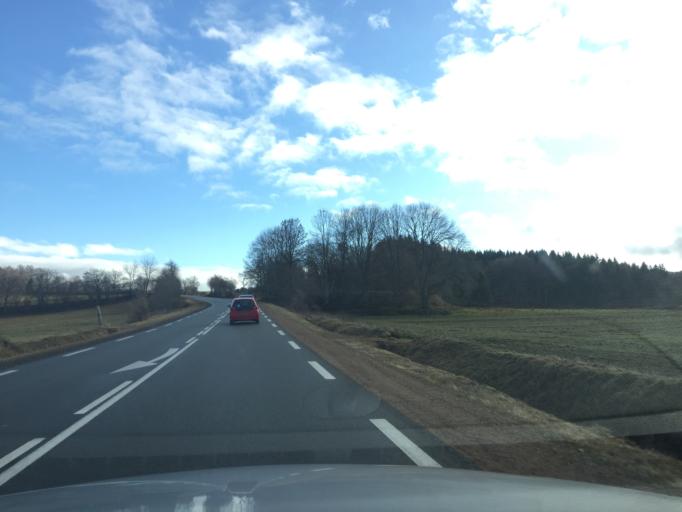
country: FR
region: Auvergne
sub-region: Departement du Puy-de-Dome
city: Saint-Ours
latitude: 45.8193
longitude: 2.9306
